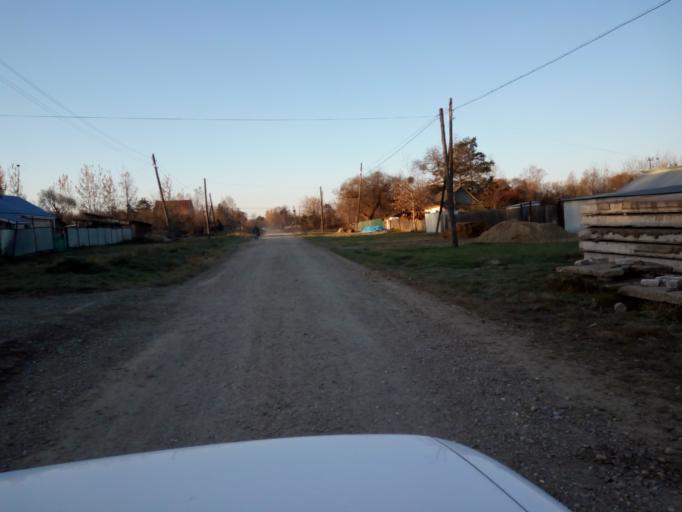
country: RU
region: Primorskiy
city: Lazo
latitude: 45.8795
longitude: 133.6526
